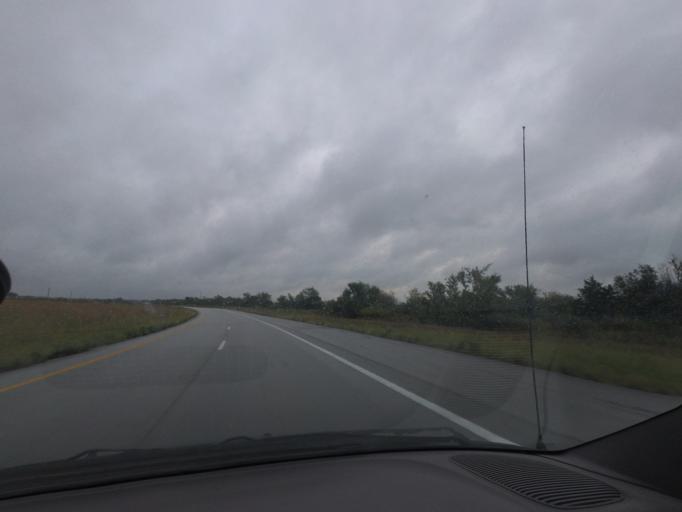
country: US
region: Missouri
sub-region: Marion County
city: Monroe City
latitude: 39.6648
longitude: -91.6773
